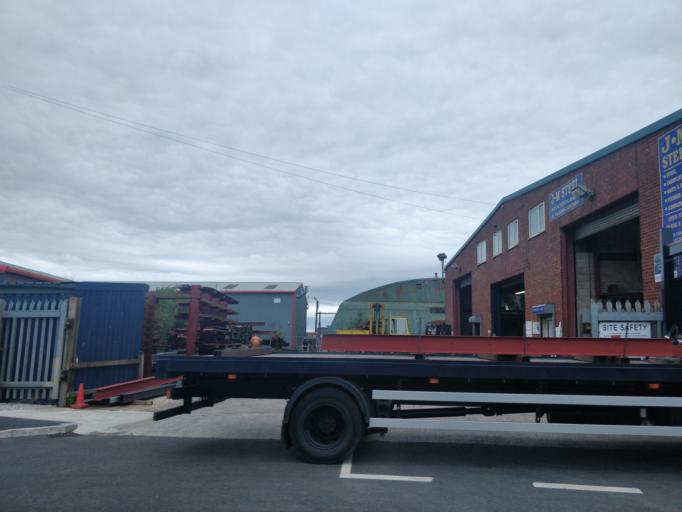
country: GB
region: England
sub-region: Lancashire
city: Ormskirk
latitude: 53.5914
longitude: -2.8627
